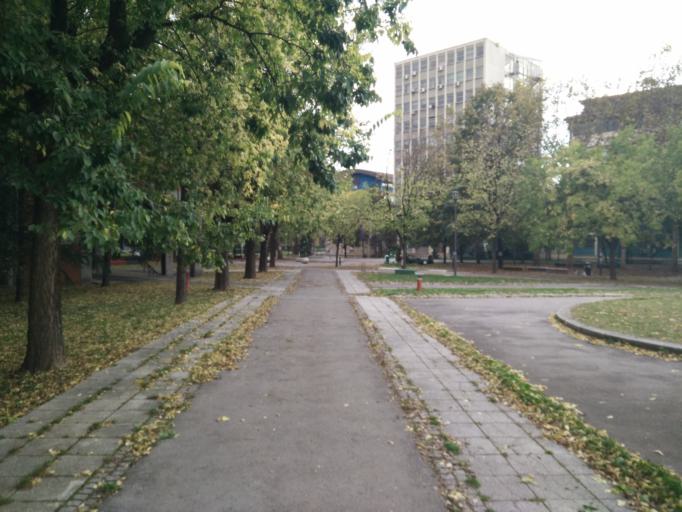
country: RS
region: Autonomna Pokrajina Vojvodina
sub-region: Juznobacki Okrug
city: Novi Sad
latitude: 45.2469
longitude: 19.8527
